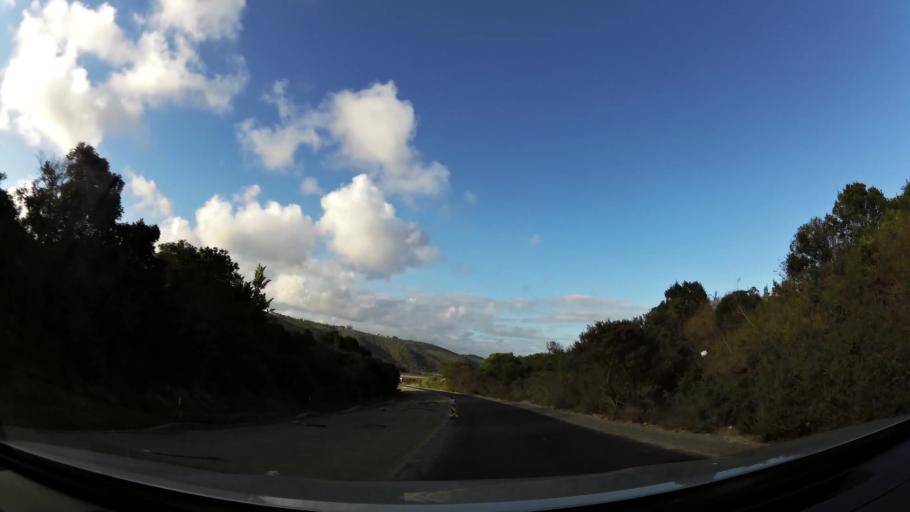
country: ZA
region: Western Cape
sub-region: Eden District Municipality
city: George
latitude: -33.9957
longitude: 22.6153
